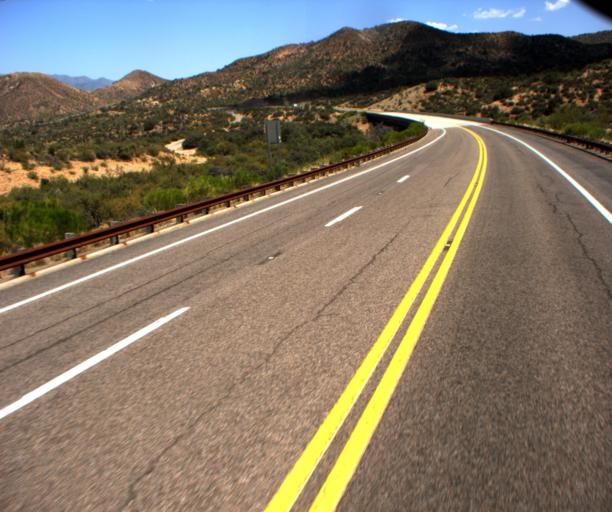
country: US
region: Arizona
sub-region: Gila County
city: Miami
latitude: 33.5259
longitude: -110.9122
